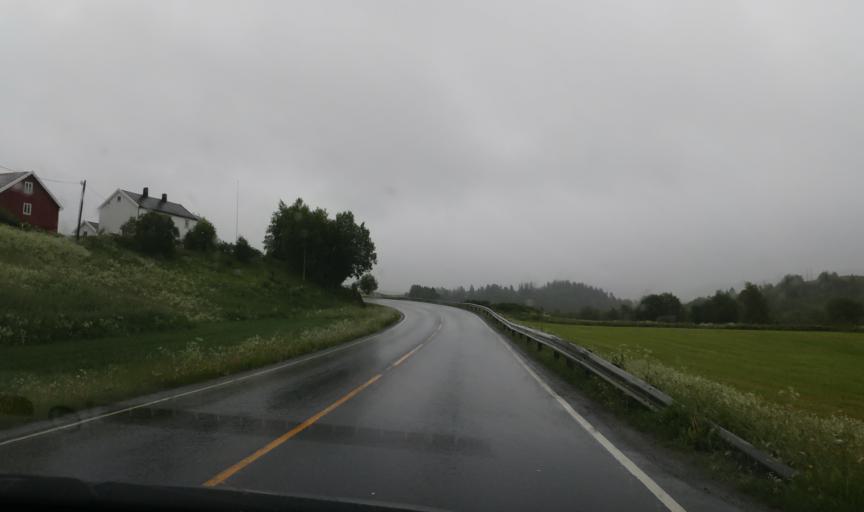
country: NO
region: Sor-Trondelag
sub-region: Selbu
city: Mebonden
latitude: 63.3889
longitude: 11.0720
